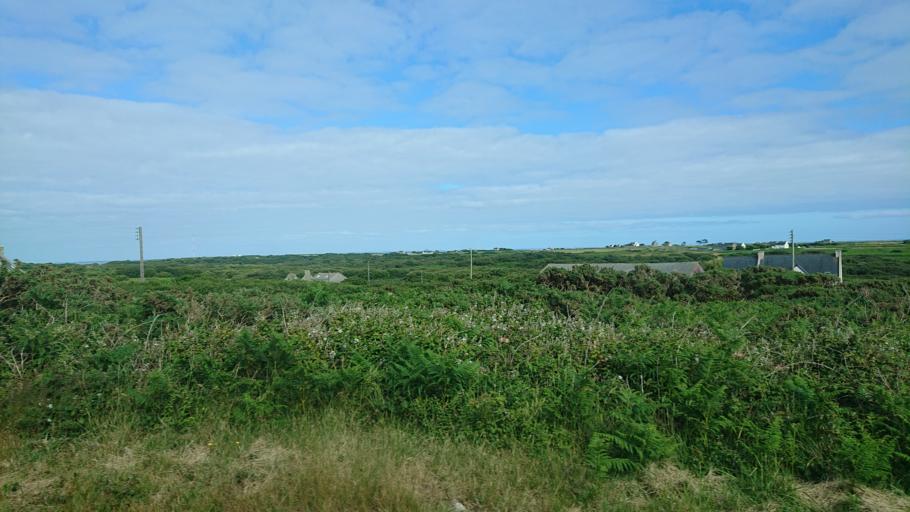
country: FR
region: Brittany
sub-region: Departement du Finistere
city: Porspoder
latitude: 48.4651
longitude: -5.0790
